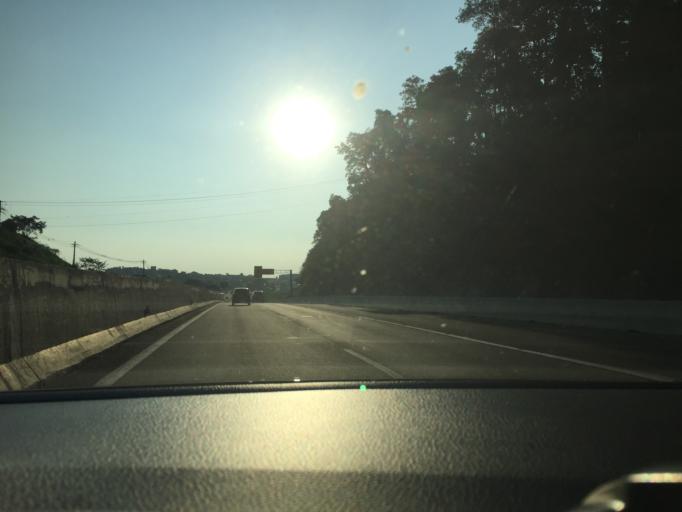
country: BR
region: Sao Paulo
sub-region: Louveira
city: Louveira
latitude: -23.0940
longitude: -46.9636
